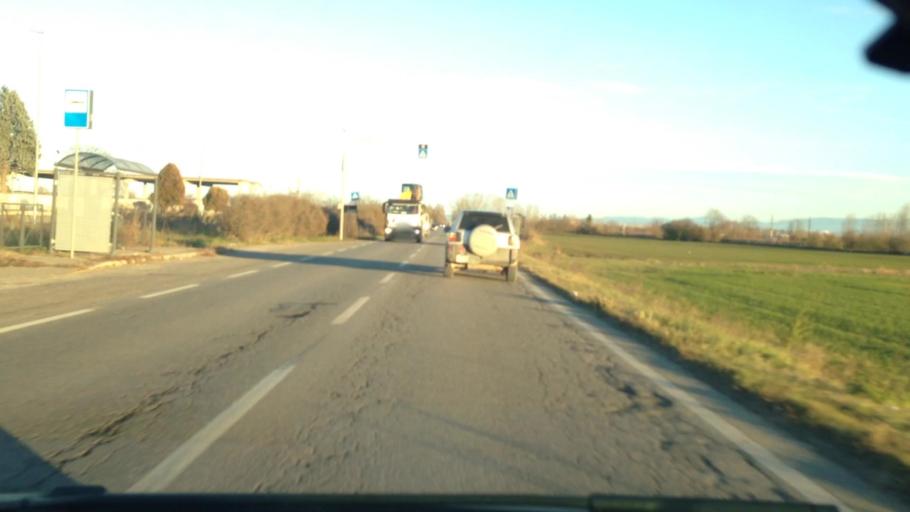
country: IT
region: Piedmont
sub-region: Provincia di Alessandria
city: Solero
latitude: 44.9210
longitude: 8.5261
